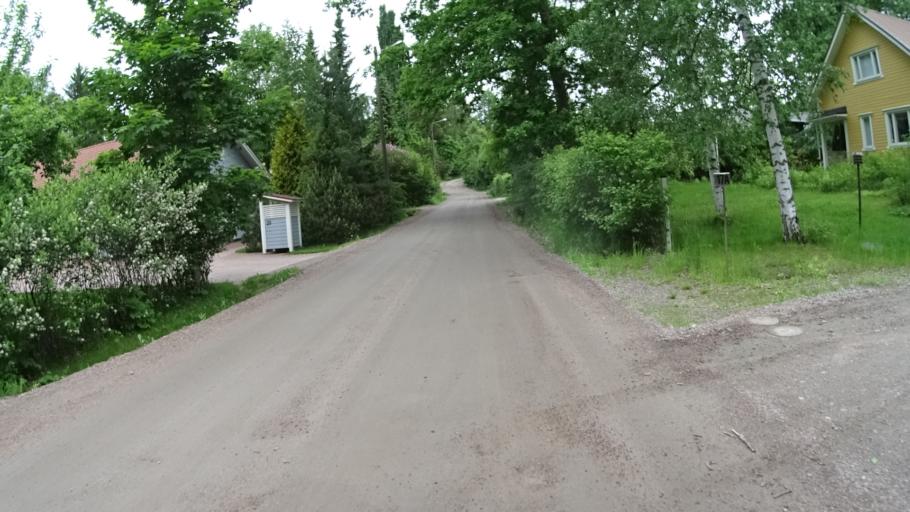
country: FI
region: Uusimaa
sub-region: Helsinki
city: Kilo
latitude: 60.2521
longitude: 24.7582
